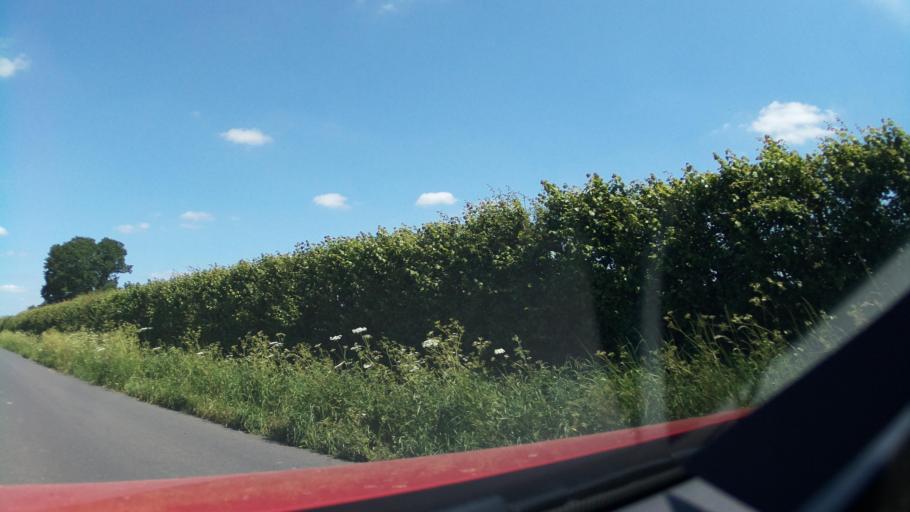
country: GB
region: England
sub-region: Wiltshire
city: Royal Wootton Bassett
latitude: 51.5134
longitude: -1.8944
